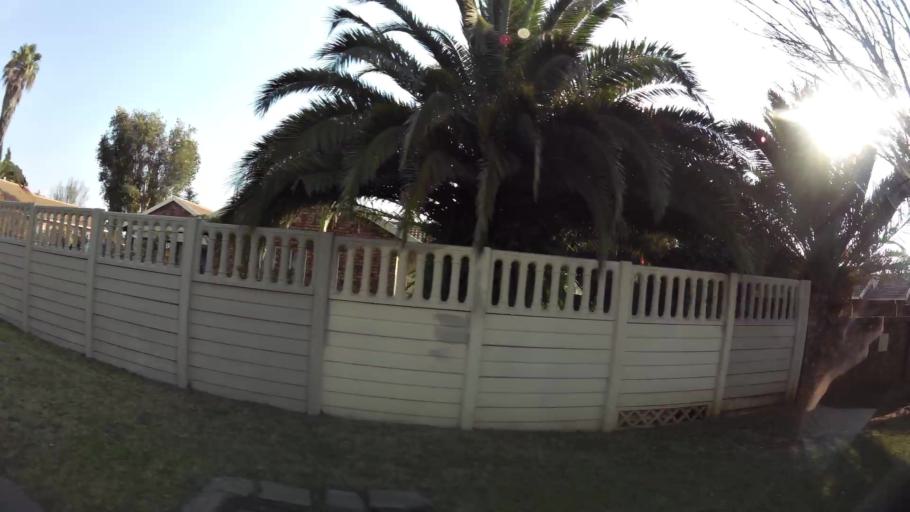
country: ZA
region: Gauteng
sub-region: Ekurhuleni Metropolitan Municipality
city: Benoni
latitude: -26.1337
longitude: 28.3675
